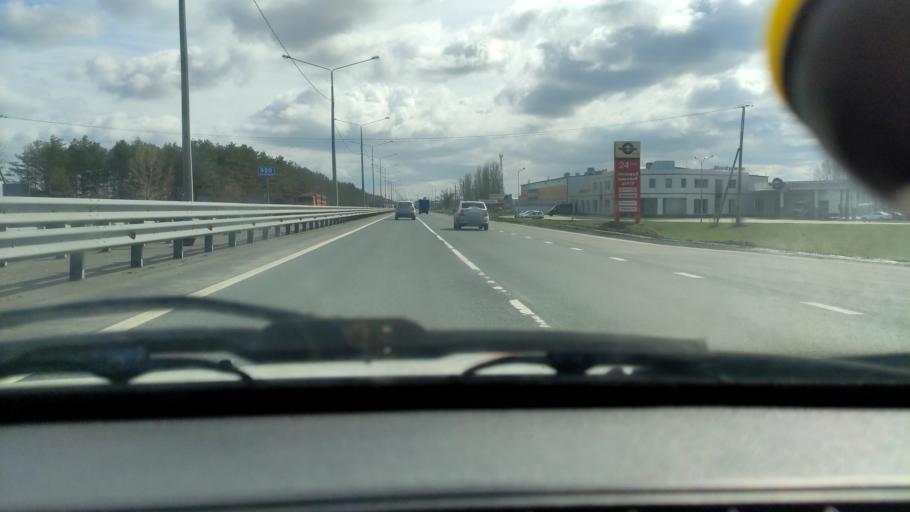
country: RU
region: Samara
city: Zhigulevsk
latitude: 53.5129
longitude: 49.5888
